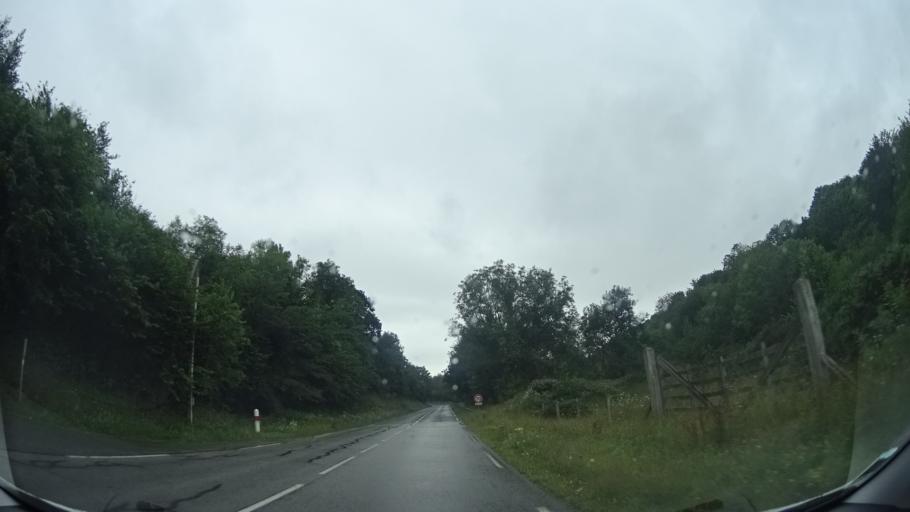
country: FR
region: Lower Normandy
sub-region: Departement de la Manche
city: Beaumont-Hague
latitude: 49.6107
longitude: -1.7898
